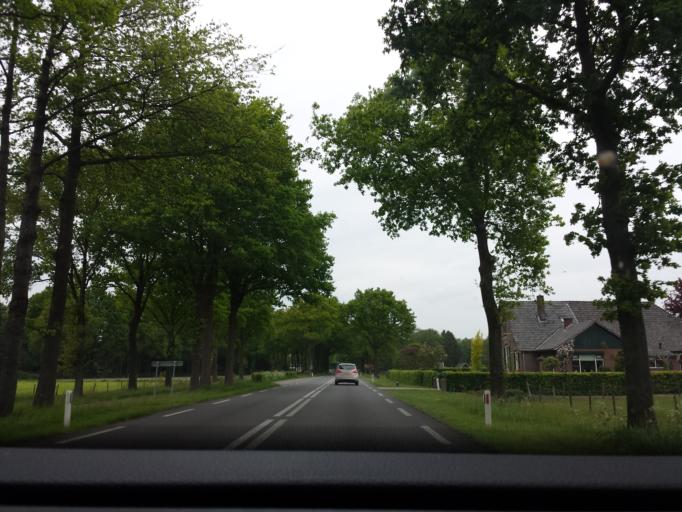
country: NL
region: Gelderland
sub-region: Gemeente Bronckhorst
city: Hengelo
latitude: 52.0896
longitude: 6.3154
